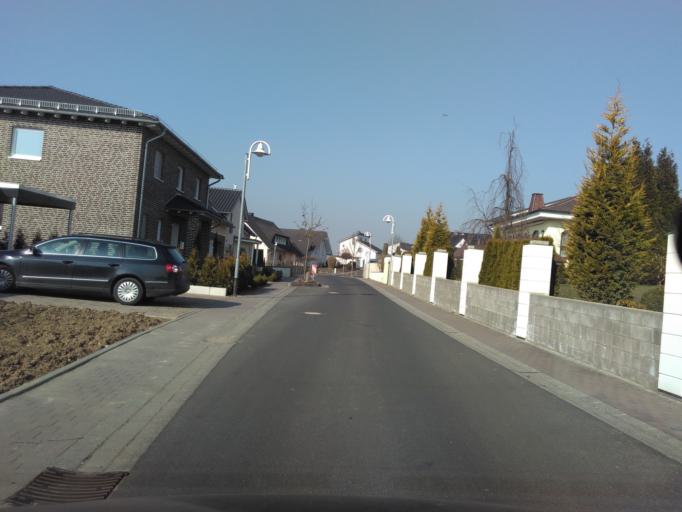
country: DE
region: Rheinland-Pfalz
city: Bannberscheid
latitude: 50.4675
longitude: 7.8284
